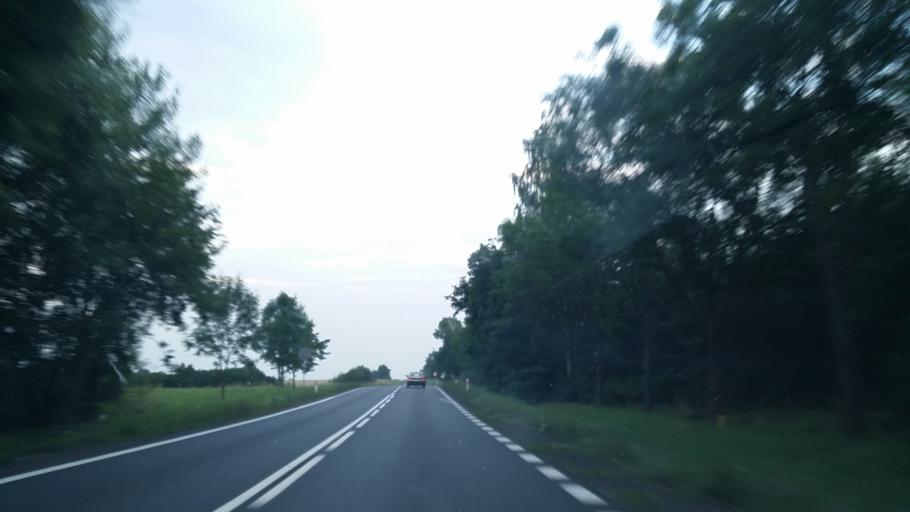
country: PL
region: Lower Silesian Voivodeship
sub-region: Powiat lubinski
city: Osiek
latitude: 51.3418
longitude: 16.2887
